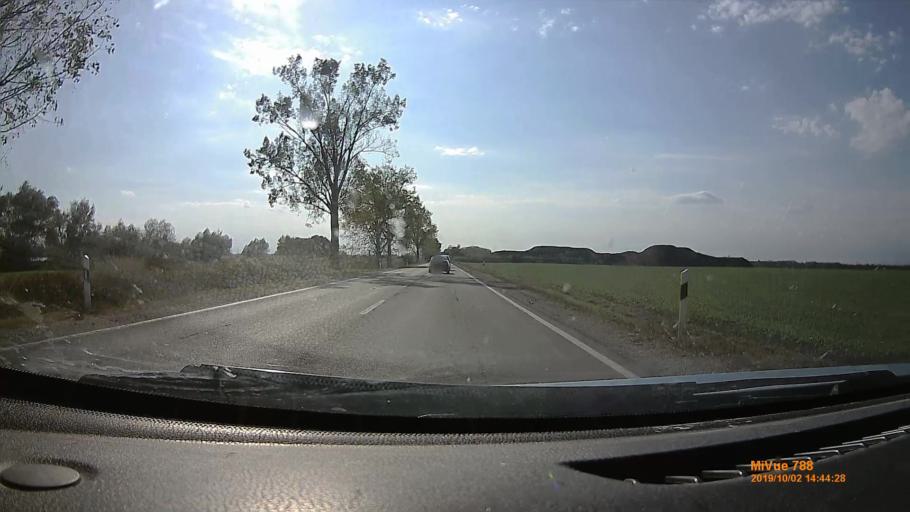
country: HU
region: Heves
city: Szihalom
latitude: 47.7670
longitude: 20.4526
